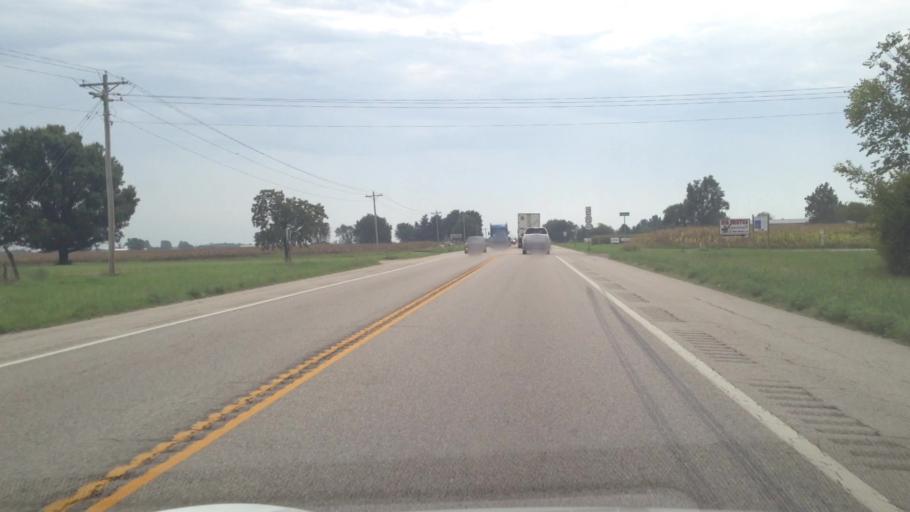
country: US
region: Kansas
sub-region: Crawford County
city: Pittsburg
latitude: 37.2812
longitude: -94.7054
